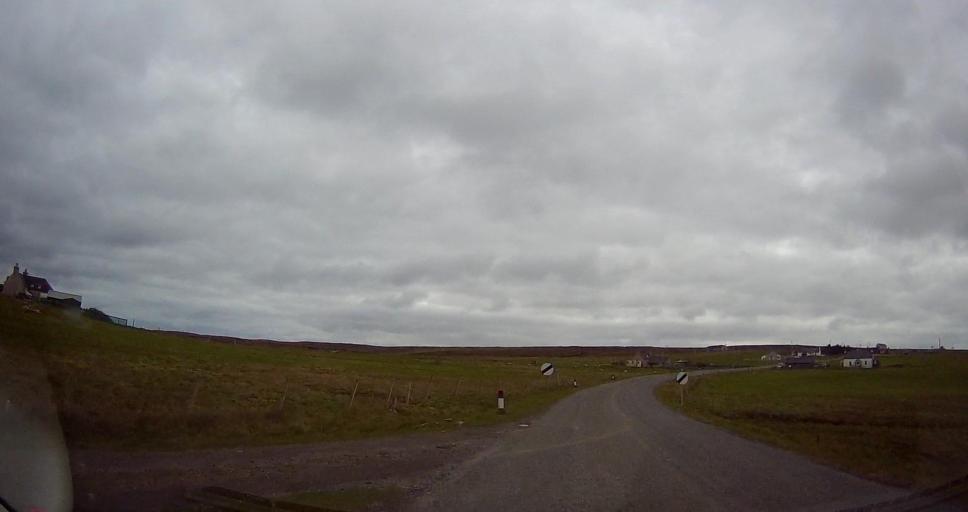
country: GB
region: Scotland
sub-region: Shetland Islands
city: Shetland
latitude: 60.6720
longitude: -0.9981
